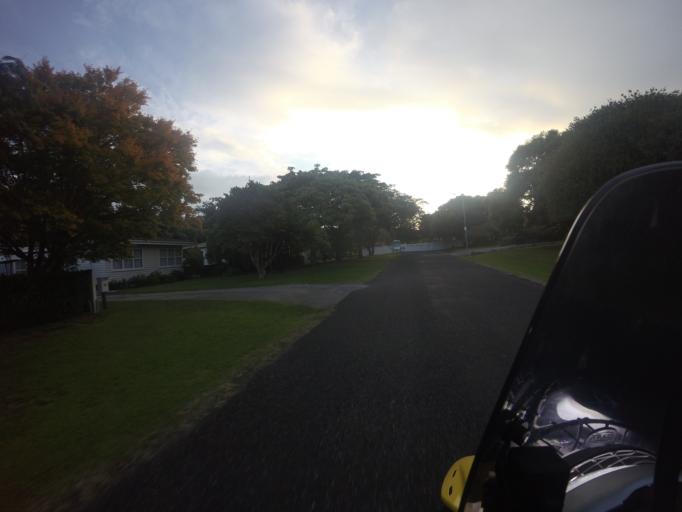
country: NZ
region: Gisborne
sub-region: Gisborne District
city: Gisborne
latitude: -38.6653
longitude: 178.0437
